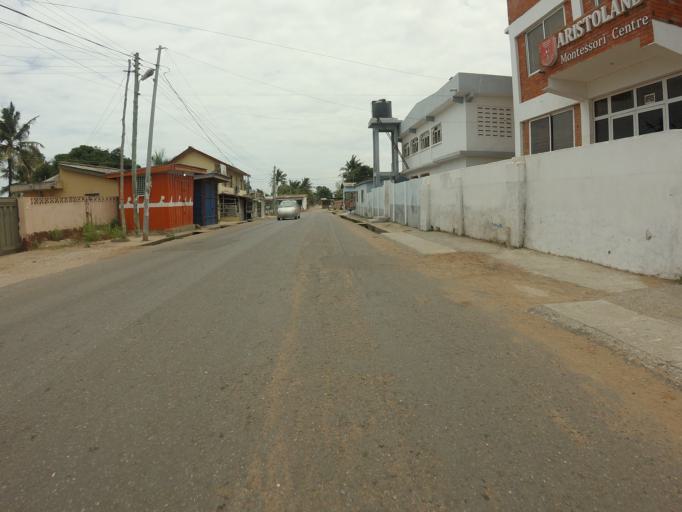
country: GH
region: Greater Accra
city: Nungua
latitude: 5.6038
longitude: -0.0893
